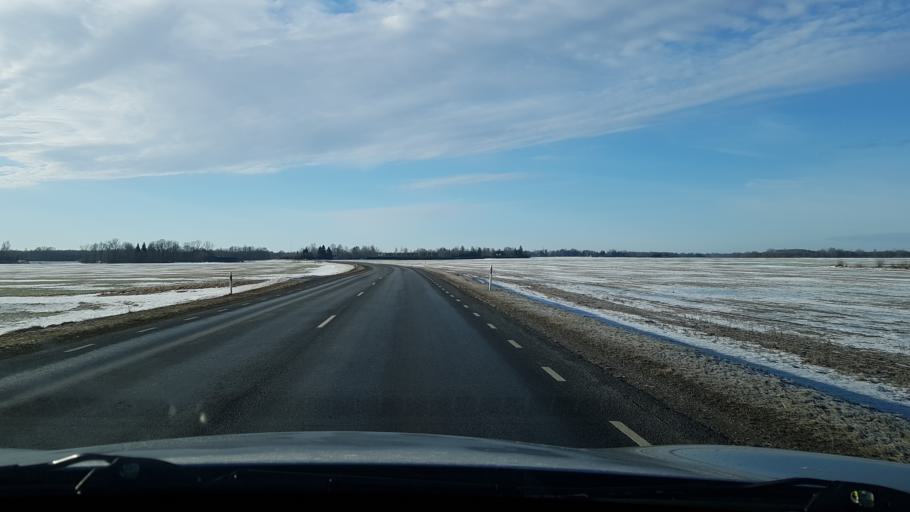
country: EE
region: Viljandimaa
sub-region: Vohma linn
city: Vohma
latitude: 58.6483
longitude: 25.5849
